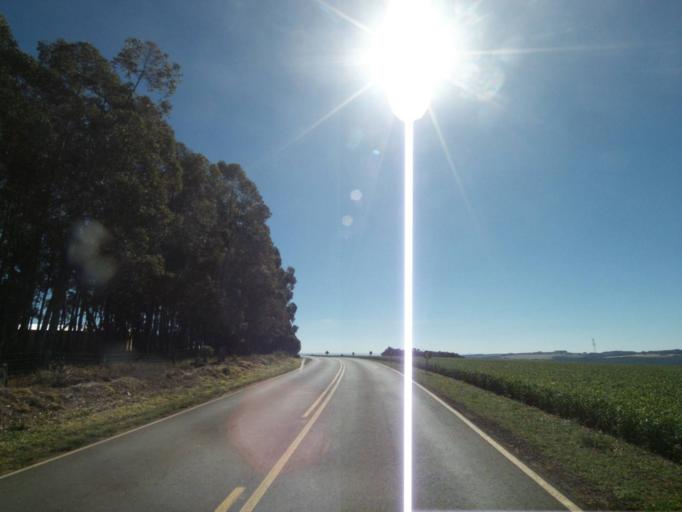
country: BR
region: Parana
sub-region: Tibagi
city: Tibagi
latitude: -24.5546
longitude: -50.2907
